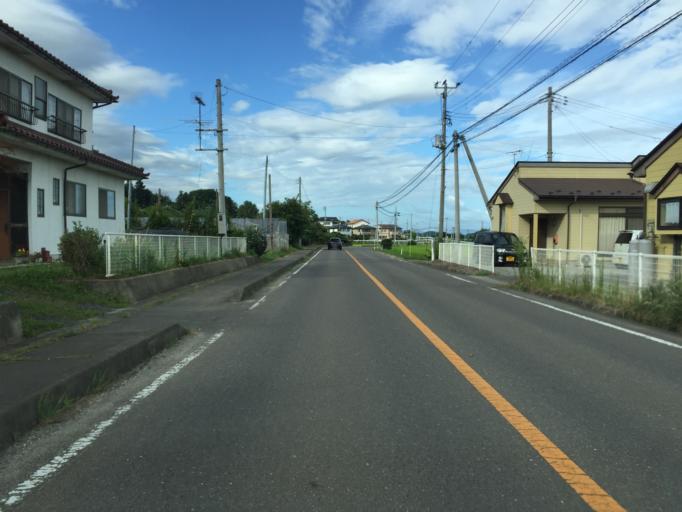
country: JP
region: Fukushima
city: Motomiya
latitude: 37.5405
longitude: 140.3756
